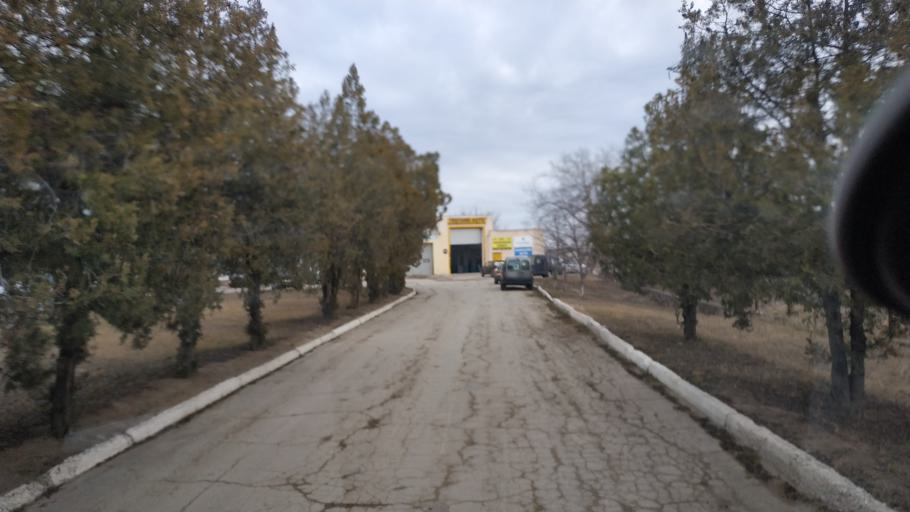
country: MD
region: Criuleni
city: Criuleni
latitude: 47.2233
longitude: 29.1500
